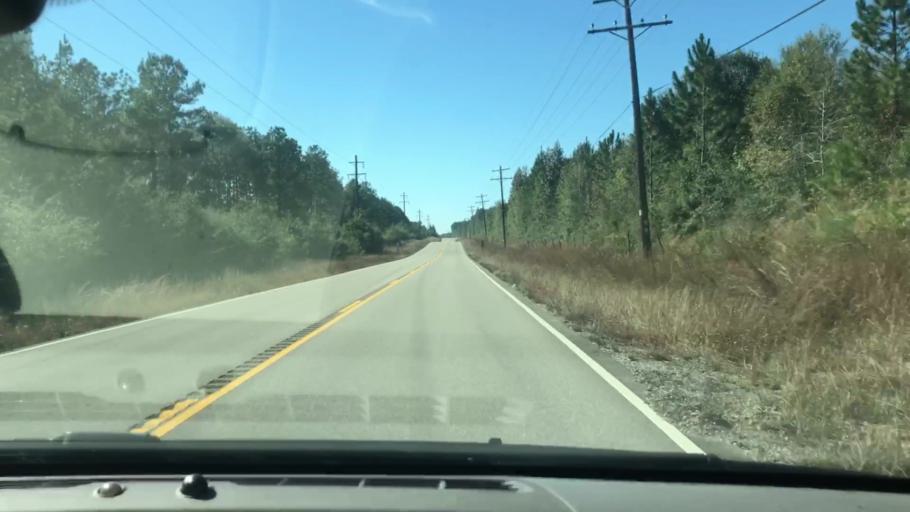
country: US
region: Louisiana
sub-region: Saint Tammany Parish
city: Abita Springs
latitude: 30.5314
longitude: -89.9100
